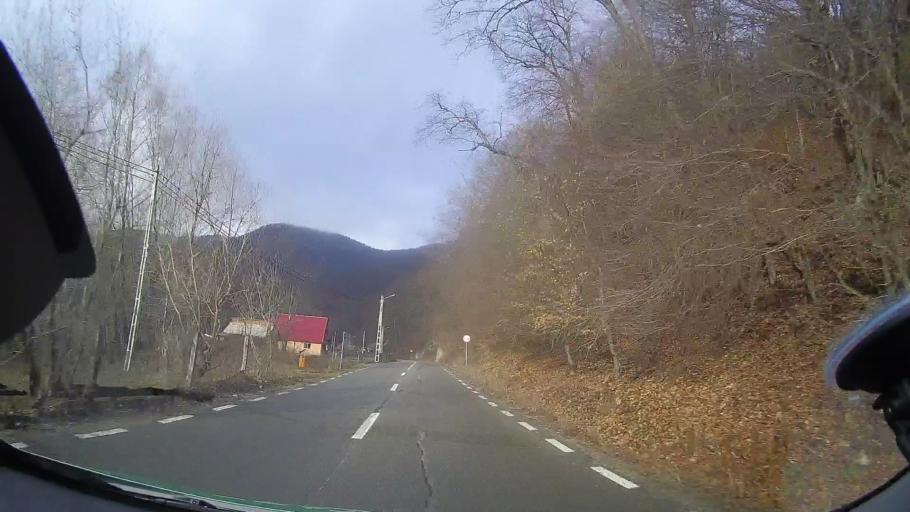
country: RO
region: Cluj
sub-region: Comuna Valea Ierii
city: Valea Ierii
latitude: 46.6438
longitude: 23.3519
